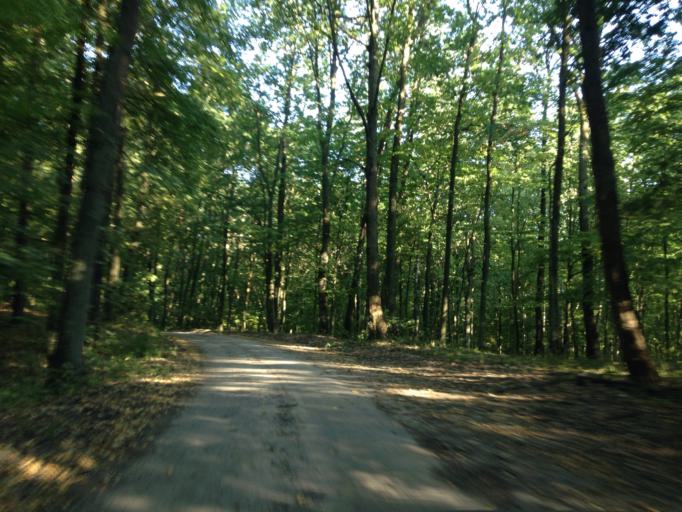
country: PL
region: Kujawsko-Pomorskie
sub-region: Powiat brodnicki
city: Gorzno
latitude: 53.2252
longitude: 19.7327
